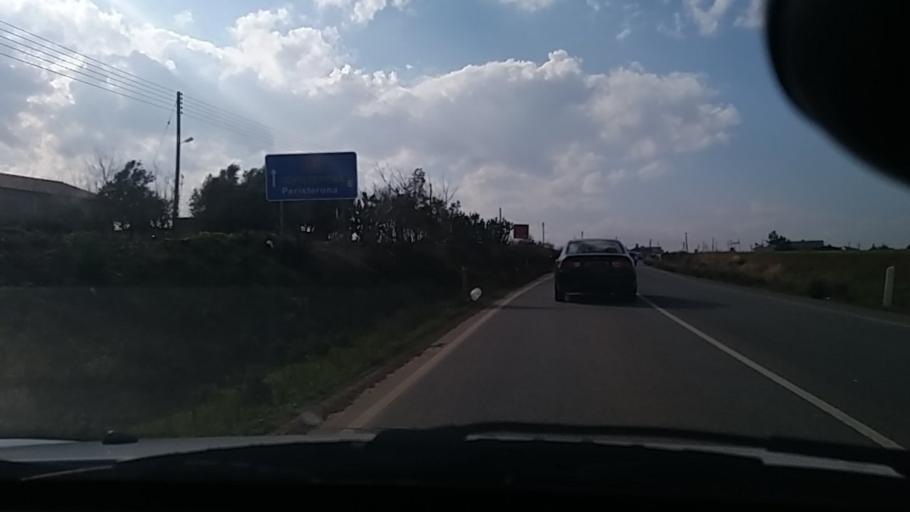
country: CY
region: Lefkosia
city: Akaki
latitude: 35.1378
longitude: 33.1535
